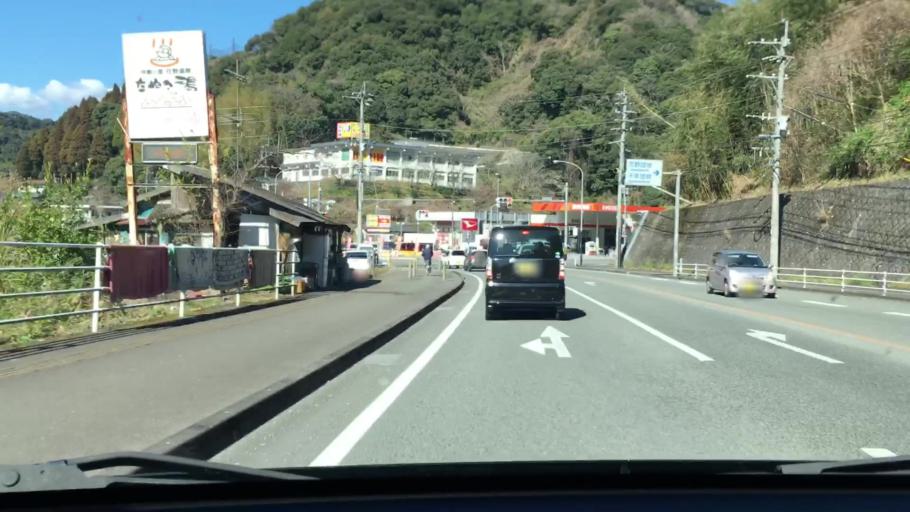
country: JP
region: Kagoshima
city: Kagoshima-shi
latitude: 31.6380
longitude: 130.5194
